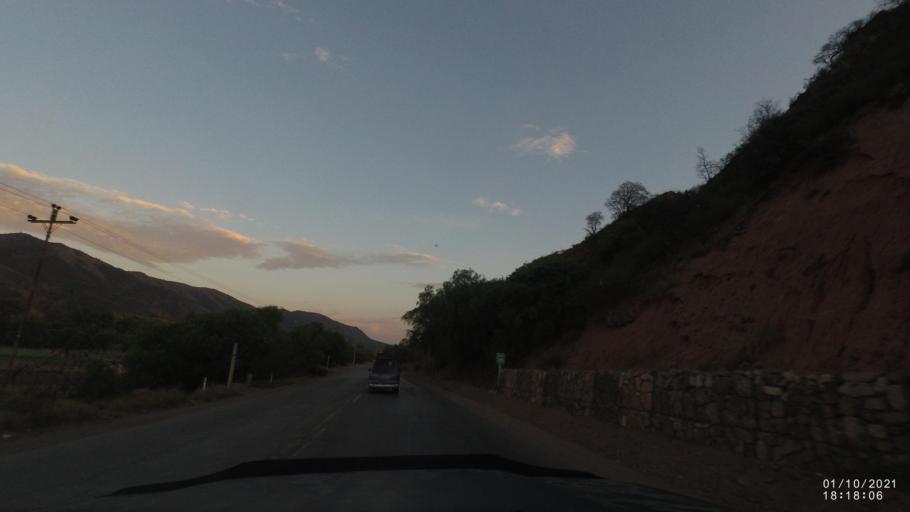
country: BO
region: Cochabamba
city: Sipe Sipe
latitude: -17.4919
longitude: -66.3384
